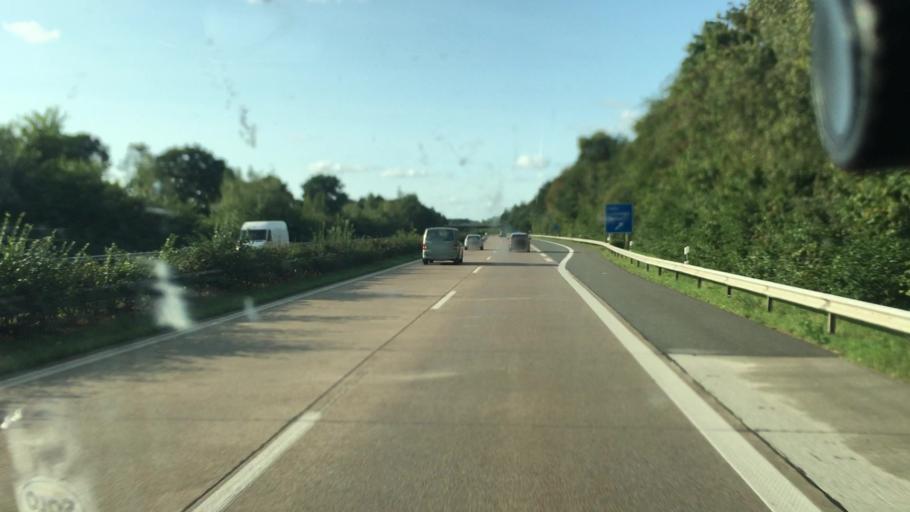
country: DE
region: Lower Saxony
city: Wiefelstede
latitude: 53.2757
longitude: 8.1581
